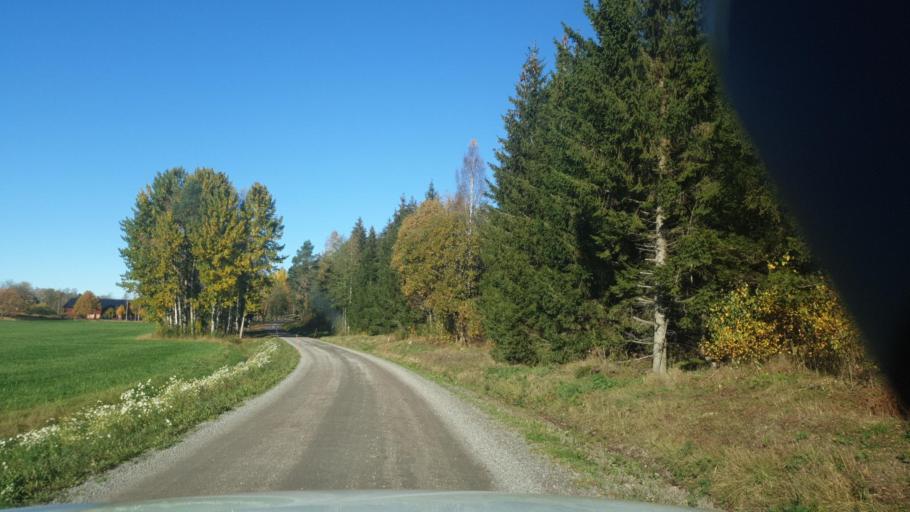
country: SE
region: Vaermland
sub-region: Arvika Kommun
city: Arvika
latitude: 59.4936
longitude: 12.7368
